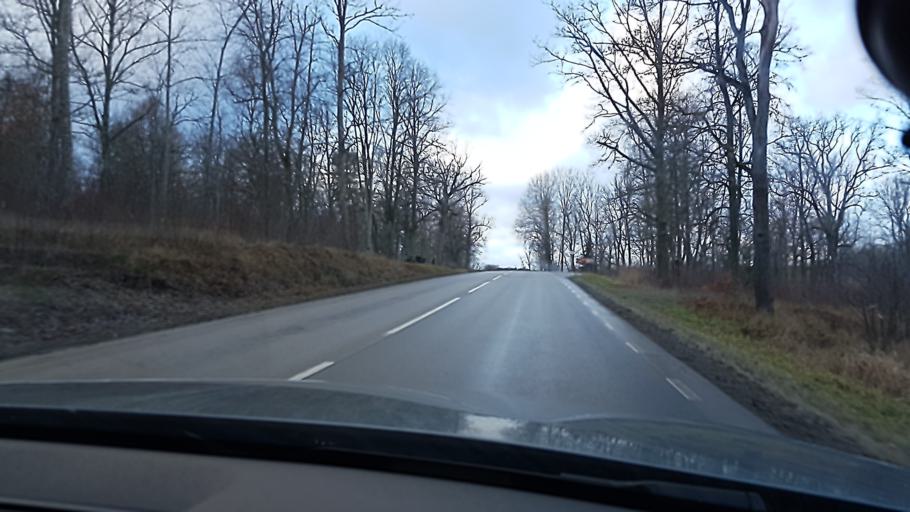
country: SE
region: OEstergoetland
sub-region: Norrkopings Kommun
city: Kimstad
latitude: 58.5523
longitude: 16.0437
